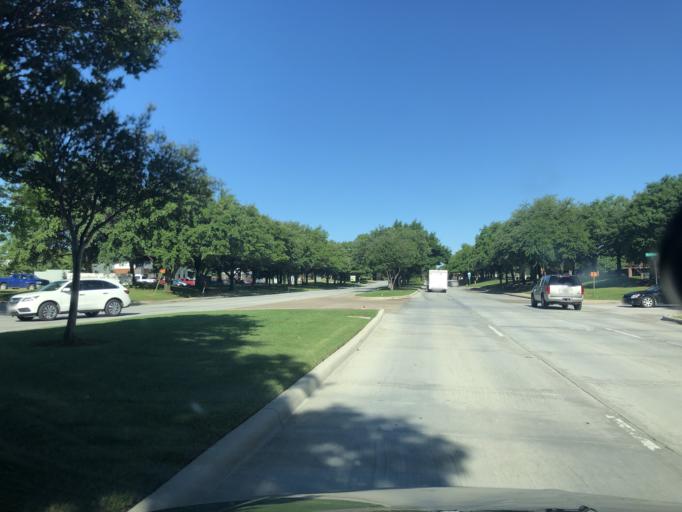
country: US
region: Texas
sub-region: Tarrant County
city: Euless
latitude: 32.8222
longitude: -97.0462
